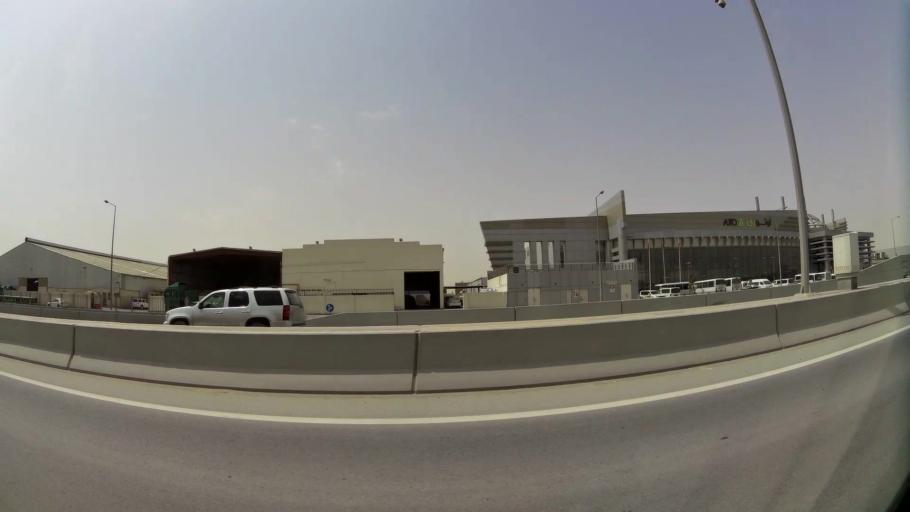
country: QA
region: Baladiyat ar Rayyan
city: Ar Rayyan
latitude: 25.2114
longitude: 51.4420
